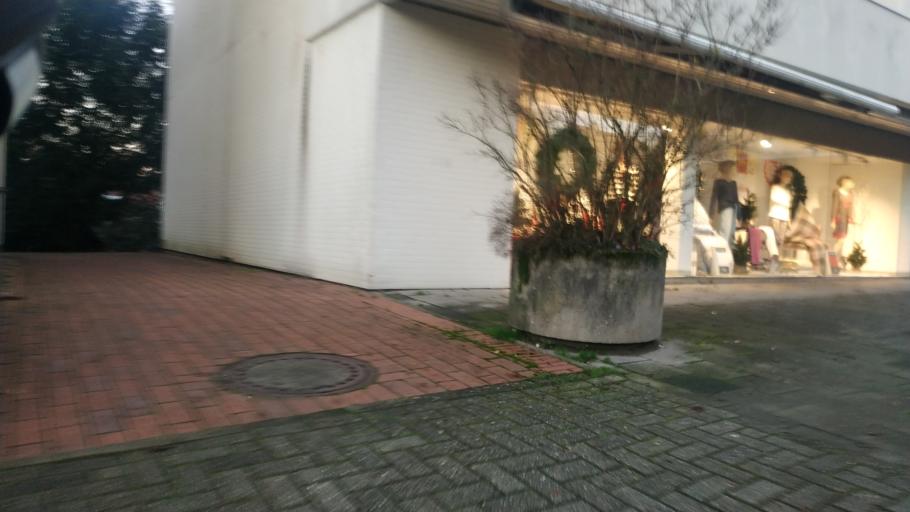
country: DE
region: North Rhine-Westphalia
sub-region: Regierungsbezirk Munster
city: Mettingen
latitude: 52.3138
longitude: 7.7795
